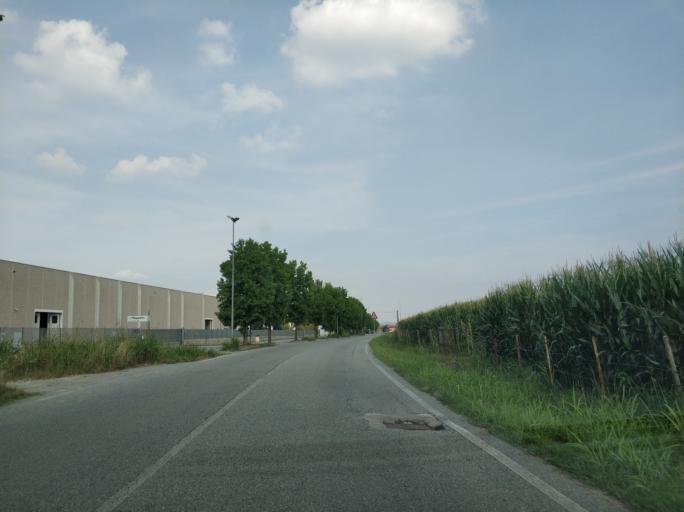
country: IT
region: Piedmont
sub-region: Provincia di Torino
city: Borgaro Torinese
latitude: 45.1519
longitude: 7.6787
